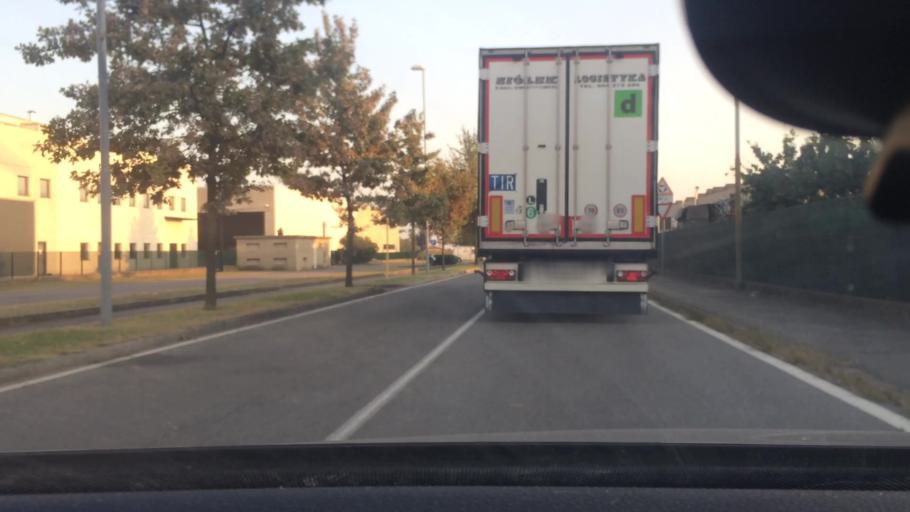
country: IT
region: Lombardy
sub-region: Provincia di Bergamo
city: Brusaporto
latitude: 45.6670
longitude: 9.7481
